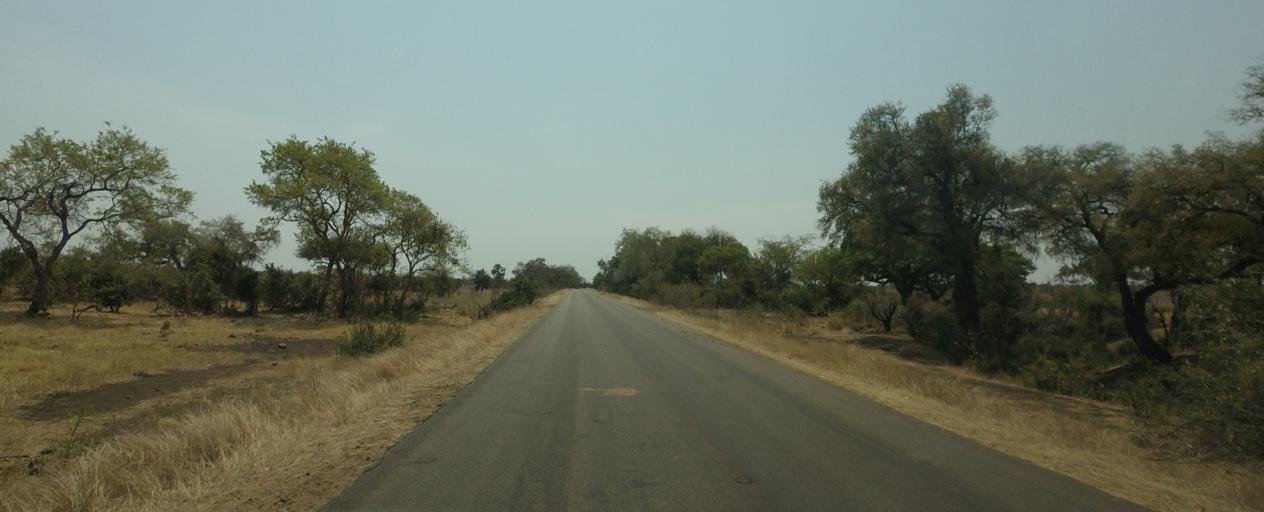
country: ZA
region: Limpopo
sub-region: Mopani District Municipality
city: Phalaborwa
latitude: -24.1632
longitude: 31.7202
